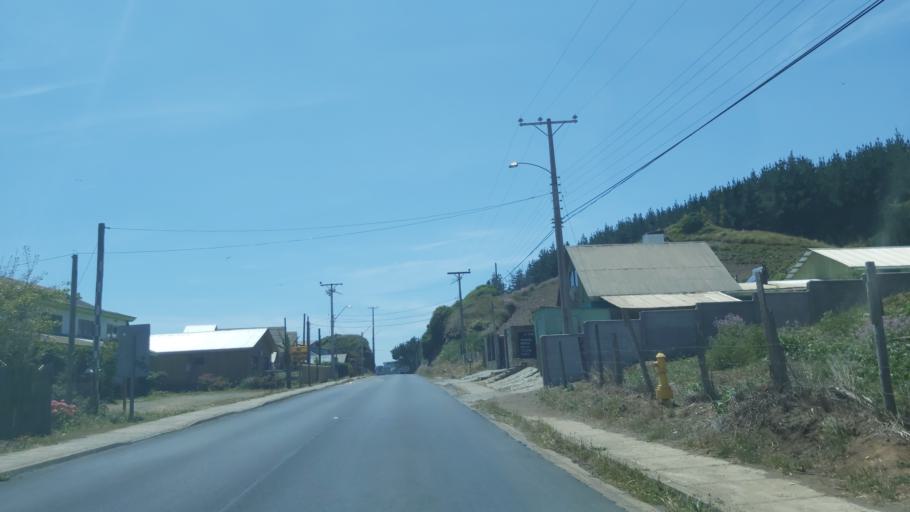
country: CL
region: Maule
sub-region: Provincia de Cauquenes
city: Cauquenes
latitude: -35.8395
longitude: -72.6275
